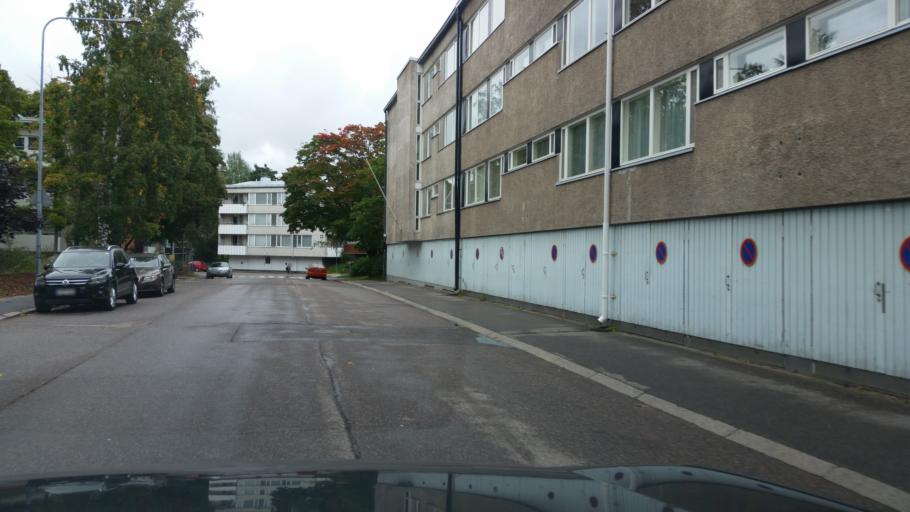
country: FI
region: Uusimaa
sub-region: Helsinki
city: Teekkarikylae
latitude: 60.2113
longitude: 24.8906
